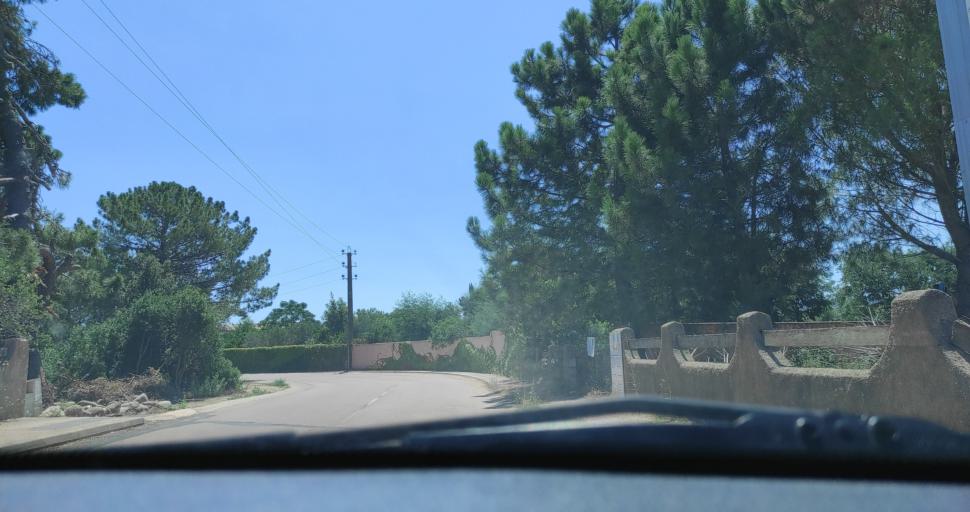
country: FR
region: Corsica
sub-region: Departement de la Corse-du-Sud
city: Porto-Vecchio
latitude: 41.6280
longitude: 9.3346
